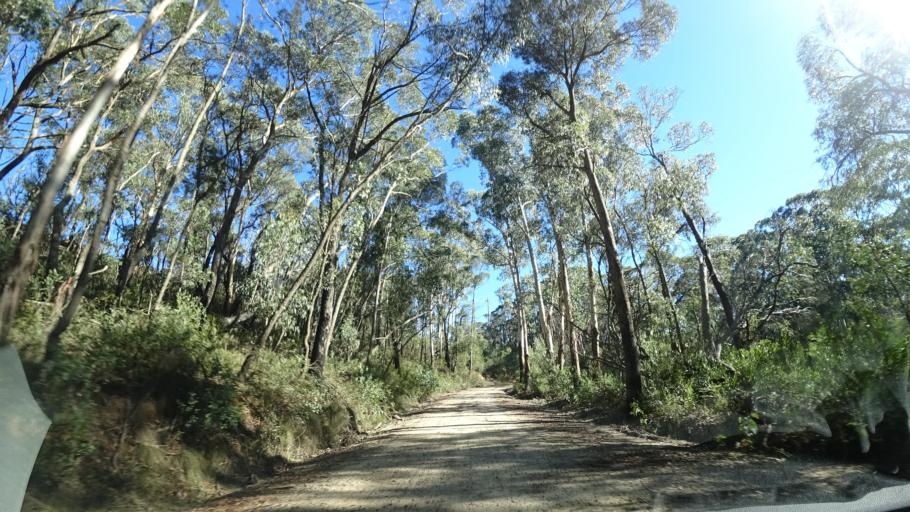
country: AU
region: New South Wales
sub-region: Lithgow
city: Lithgow
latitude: -33.4920
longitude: 150.2676
